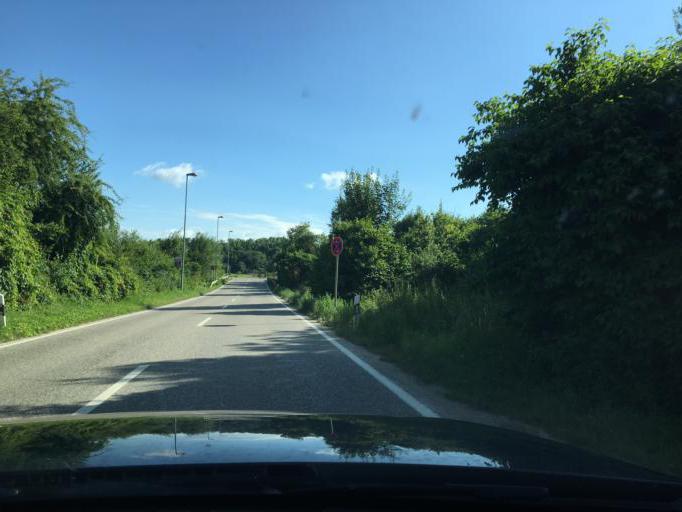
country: DE
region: Bavaria
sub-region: Upper Bavaria
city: Ingolstadt
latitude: 48.7839
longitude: 11.4301
